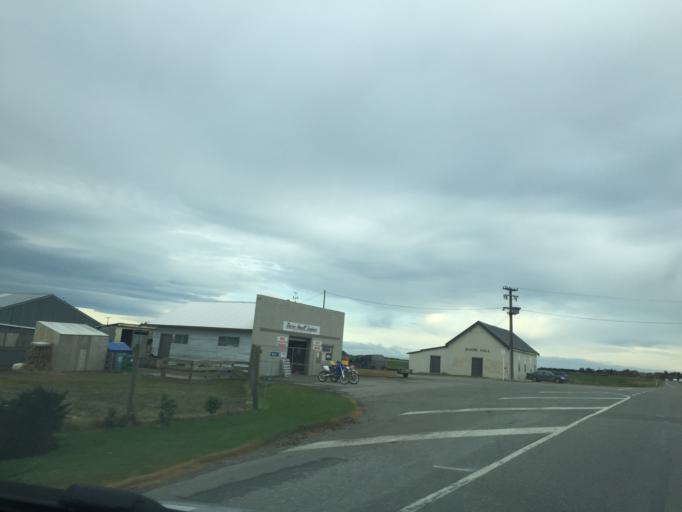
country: NZ
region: Southland
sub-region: Invercargill City
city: Invercargill
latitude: -46.3172
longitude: 168.6026
